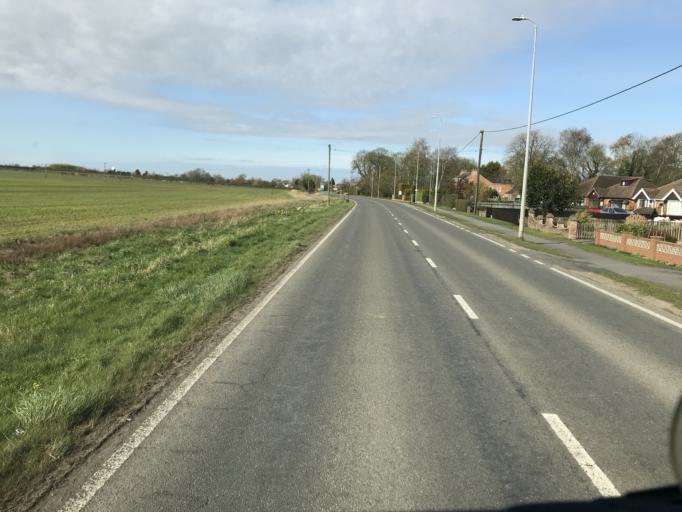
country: GB
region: England
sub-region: Lincolnshire
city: Market Rasen
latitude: 53.3884
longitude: -0.3522
